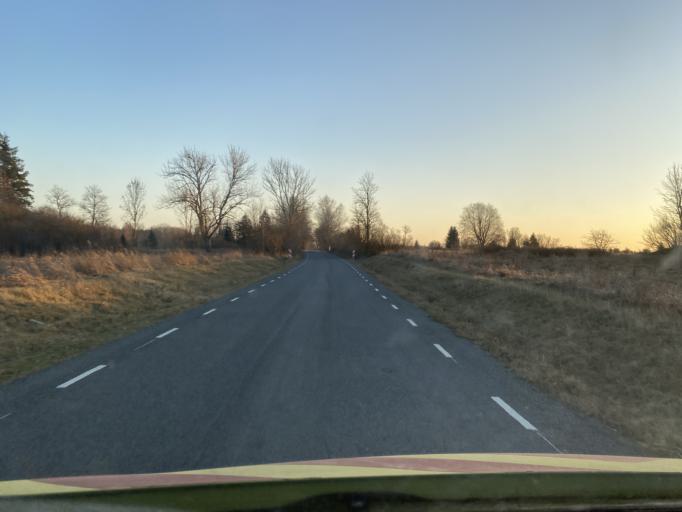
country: EE
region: Raplamaa
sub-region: Rapla vald
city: Rapla
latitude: 58.9923
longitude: 24.7240
